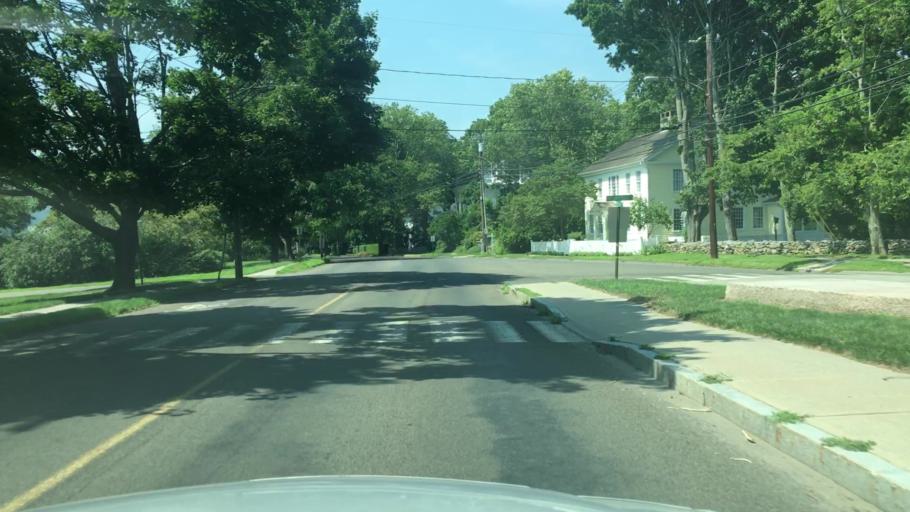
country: US
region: Connecticut
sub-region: New Haven County
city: Guilford Center
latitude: 41.2777
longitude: -72.6771
